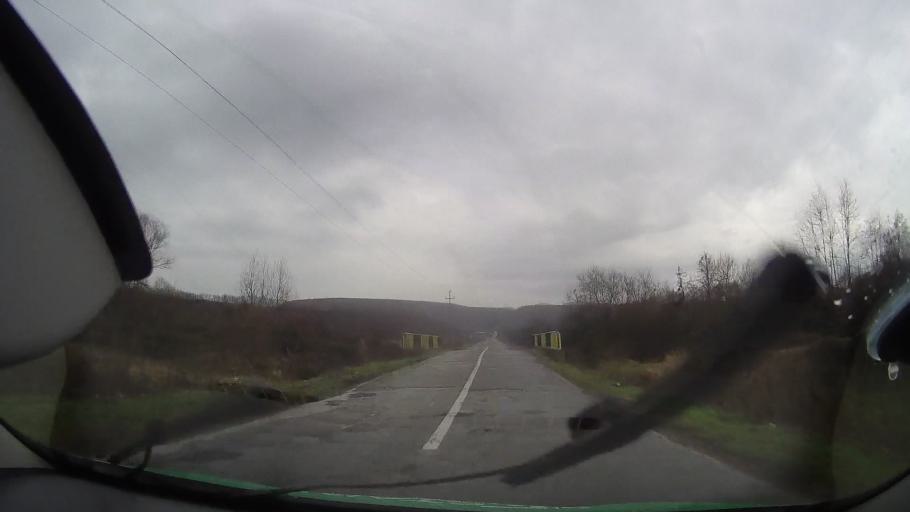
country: RO
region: Bihor
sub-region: Comuna Soimi
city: Soimi
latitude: 46.6865
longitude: 22.1080
